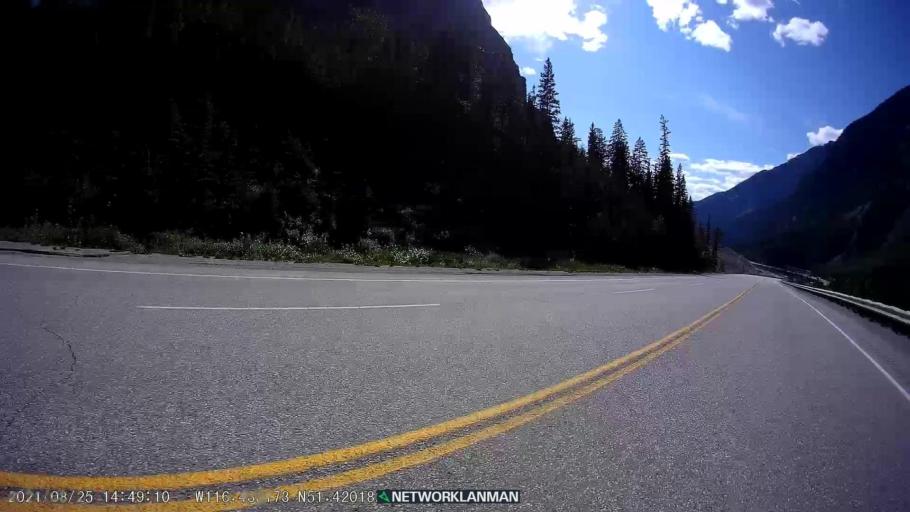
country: CA
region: Alberta
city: Lake Louise
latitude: 51.4194
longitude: -116.4298
